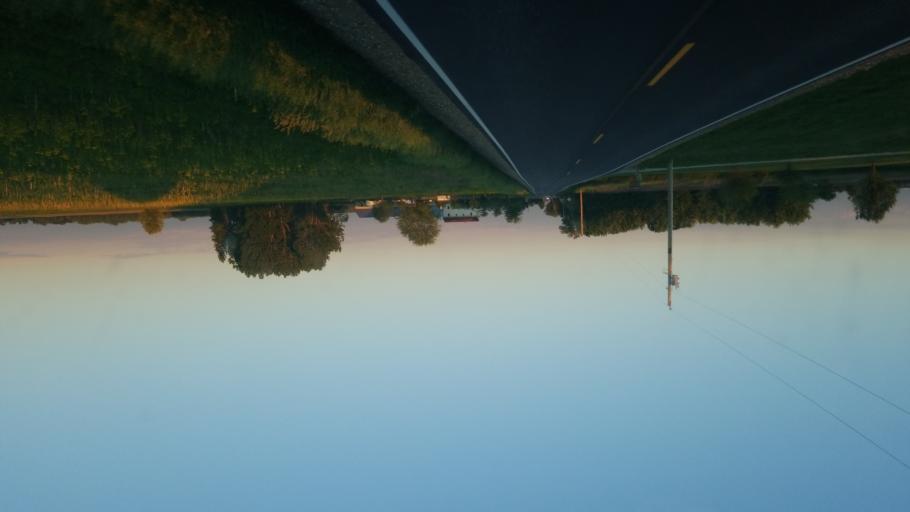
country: US
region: Indiana
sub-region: Elkhart County
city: Nappanee
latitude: 41.3614
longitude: -85.9853
